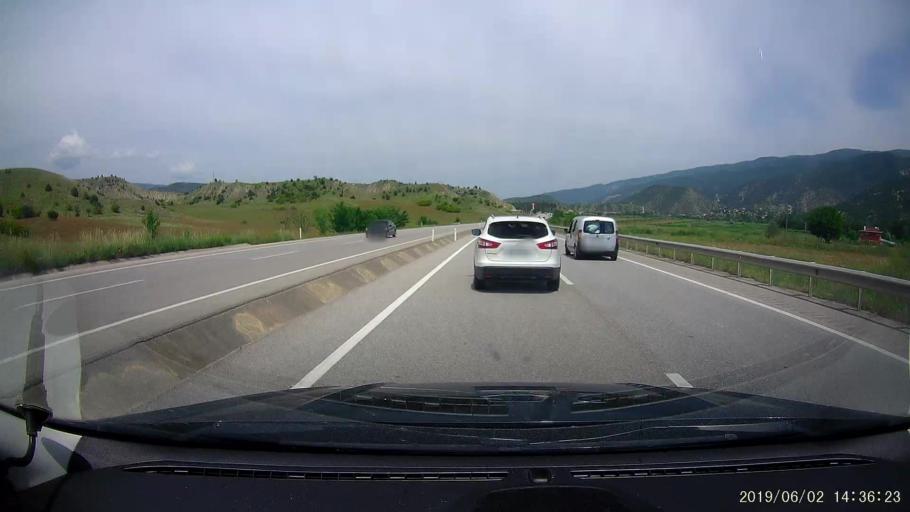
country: TR
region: Kastamonu
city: Tosya
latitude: 41.0467
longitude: 34.2341
